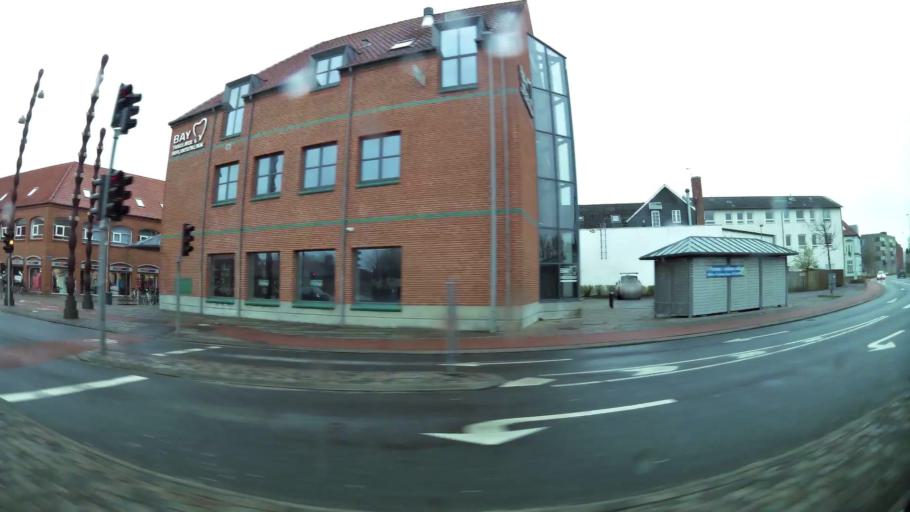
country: DK
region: Central Jutland
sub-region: Holstebro Kommune
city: Holstebro
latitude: 56.3625
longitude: 8.6188
